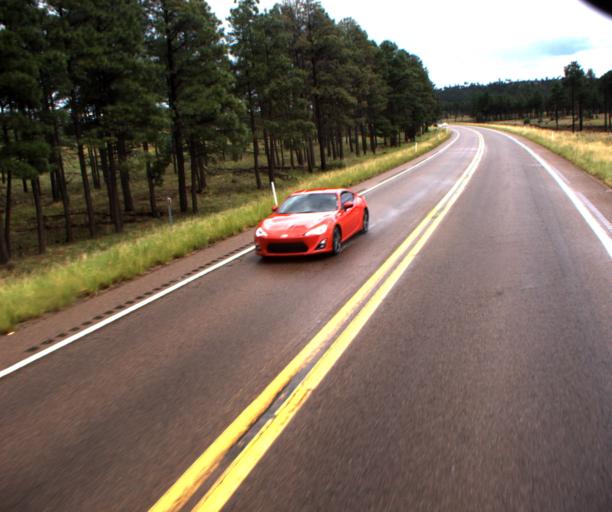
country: US
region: Arizona
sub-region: Navajo County
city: Heber-Overgaard
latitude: 34.3660
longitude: -110.4435
